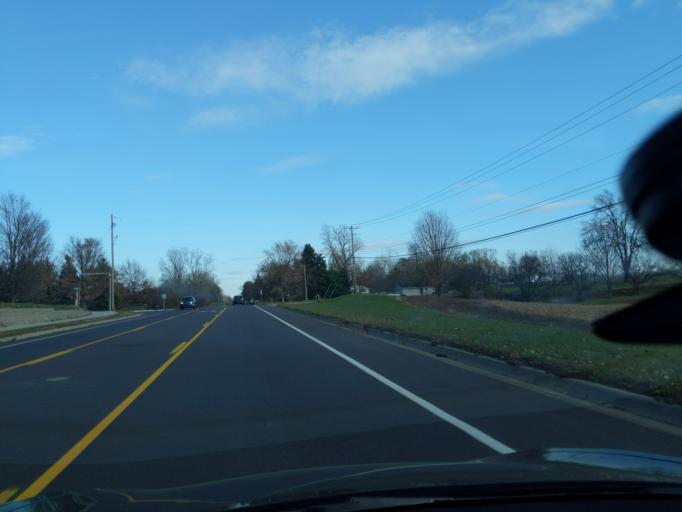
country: US
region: Michigan
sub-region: Ingham County
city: Okemos
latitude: 42.6829
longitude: -84.4228
